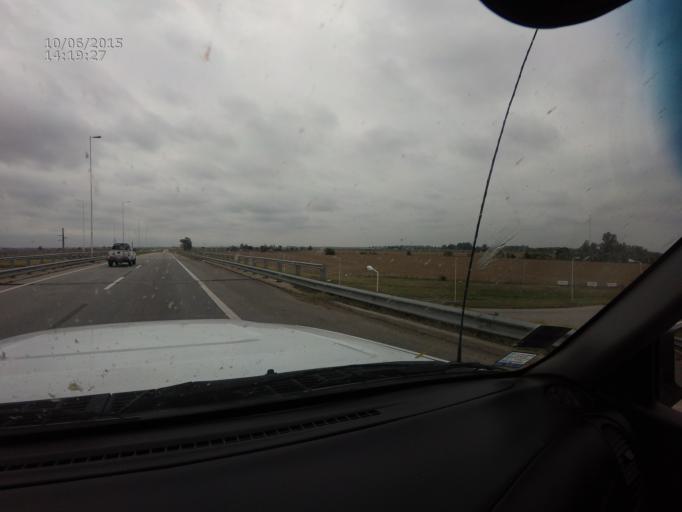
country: AR
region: Cordoba
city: Villa Maria
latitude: -32.3572
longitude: -63.2375
